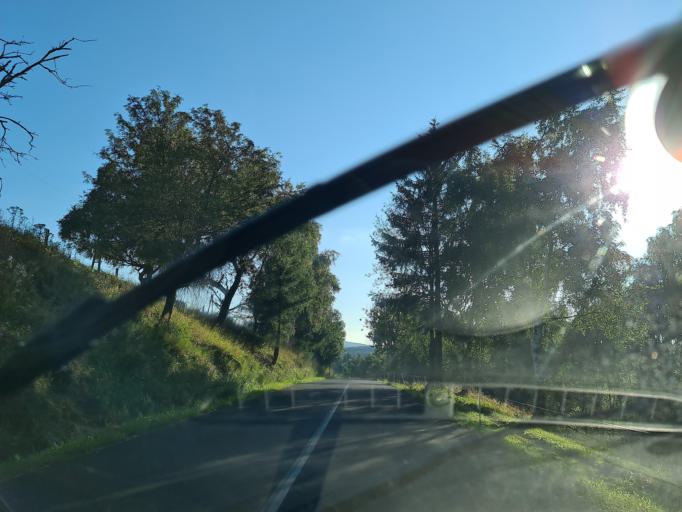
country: DE
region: Saxony
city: Deutschneudorf
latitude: 50.6219
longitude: 13.4896
